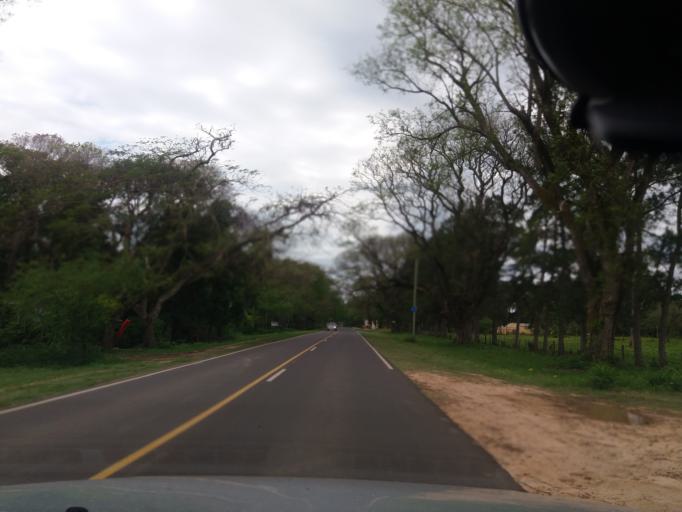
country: AR
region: Corrientes
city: Riachuelo
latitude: -27.4567
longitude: -58.6879
